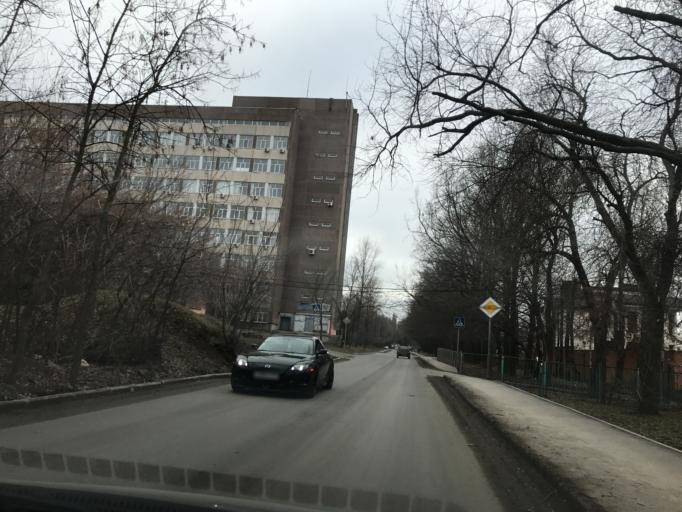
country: RU
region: Rostov
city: Rostov-na-Donu
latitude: 47.2199
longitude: 39.6267
